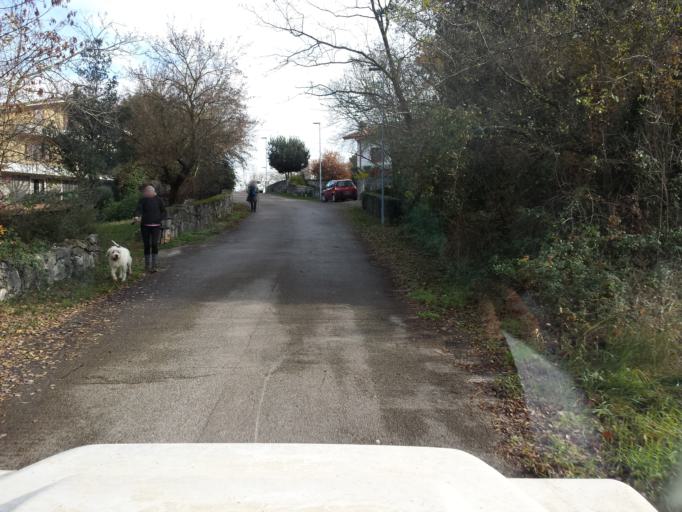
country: IT
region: Friuli Venezia Giulia
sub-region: Provincia di Gorizia
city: Savogna d'Isonzo
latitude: 45.8802
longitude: 13.5603
